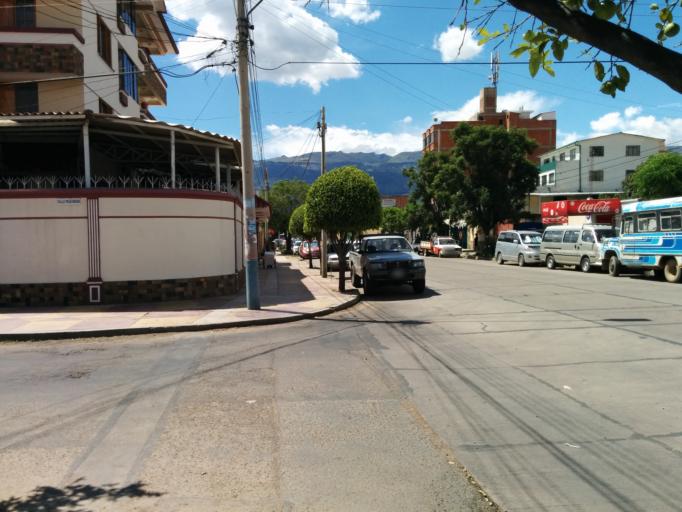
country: BO
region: Cochabamba
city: Cochabamba
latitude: -17.4016
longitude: -66.1667
